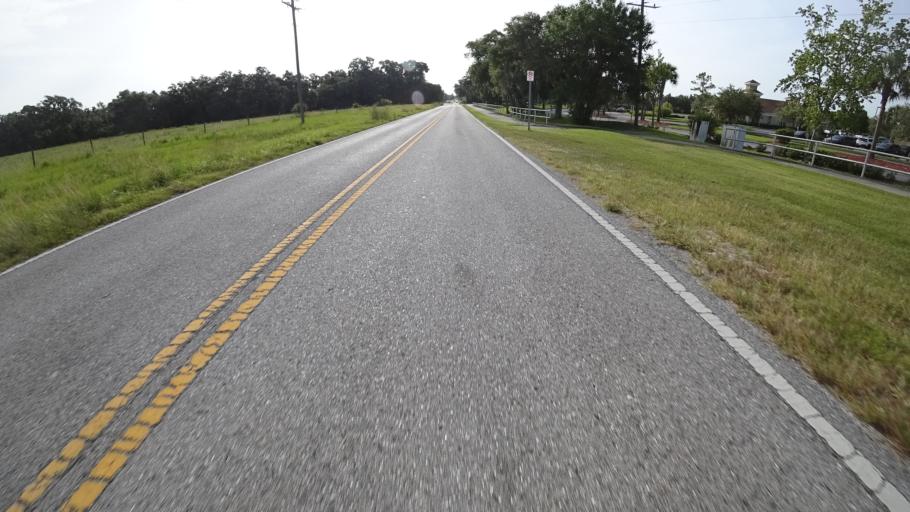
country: US
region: Florida
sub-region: Manatee County
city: Ellenton
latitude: 27.5469
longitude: -82.5071
